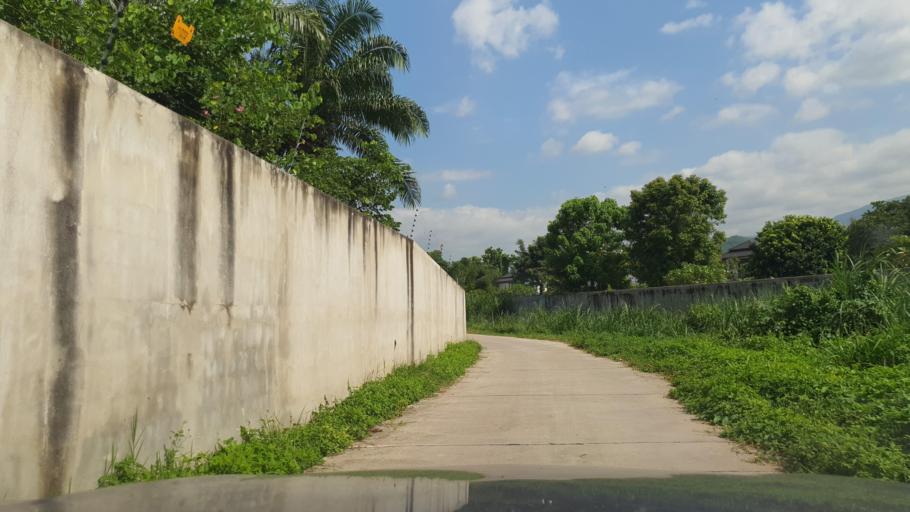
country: TH
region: Chiang Mai
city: Hang Dong
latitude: 18.7208
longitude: 98.9139
